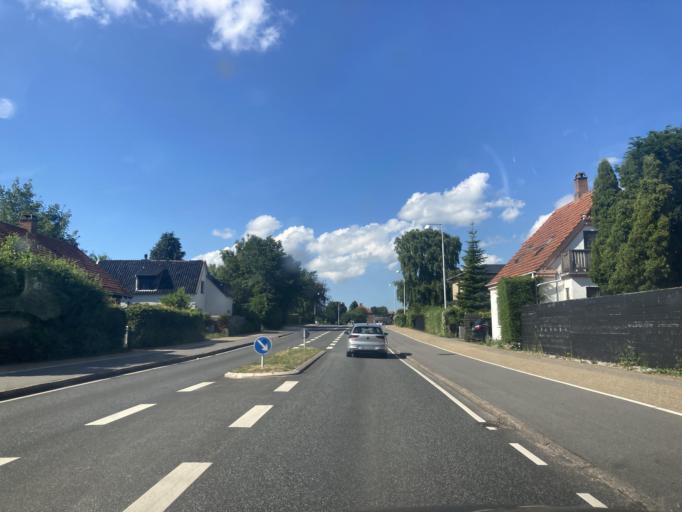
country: DK
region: Capital Region
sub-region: Rudersdal Kommune
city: Birkerod
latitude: 55.8342
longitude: 12.4305
